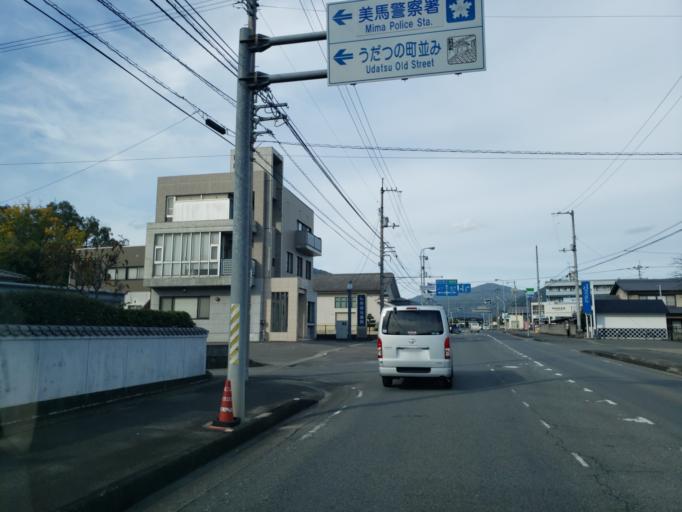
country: JP
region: Tokushima
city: Wakimachi
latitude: 34.0647
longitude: 134.1695
